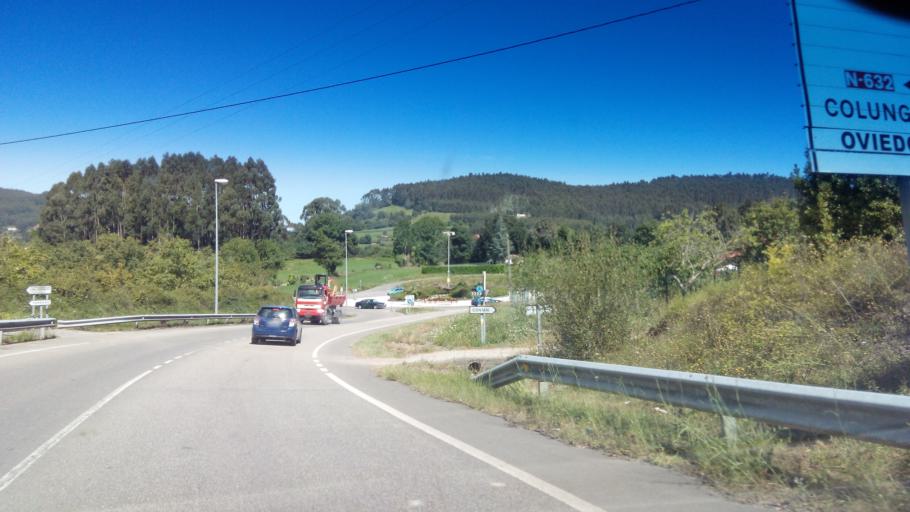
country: ES
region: Asturias
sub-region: Province of Asturias
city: Colunga
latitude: 43.4826
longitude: -5.2555
